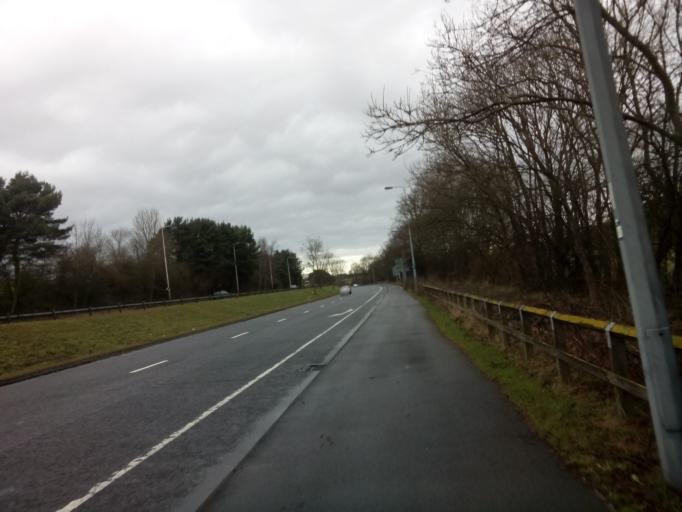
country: GB
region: England
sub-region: County Durham
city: Sacriston
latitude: 54.8112
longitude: -1.5888
